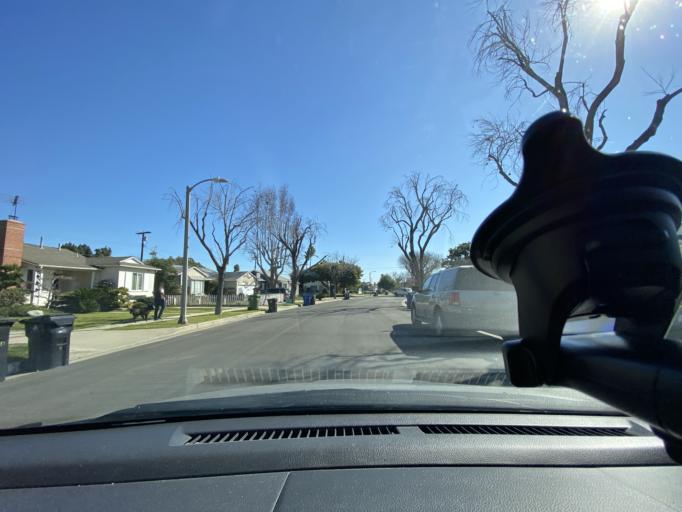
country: US
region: California
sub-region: Los Angeles County
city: Westwood, Los Angeles
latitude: 34.0284
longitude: -118.4369
